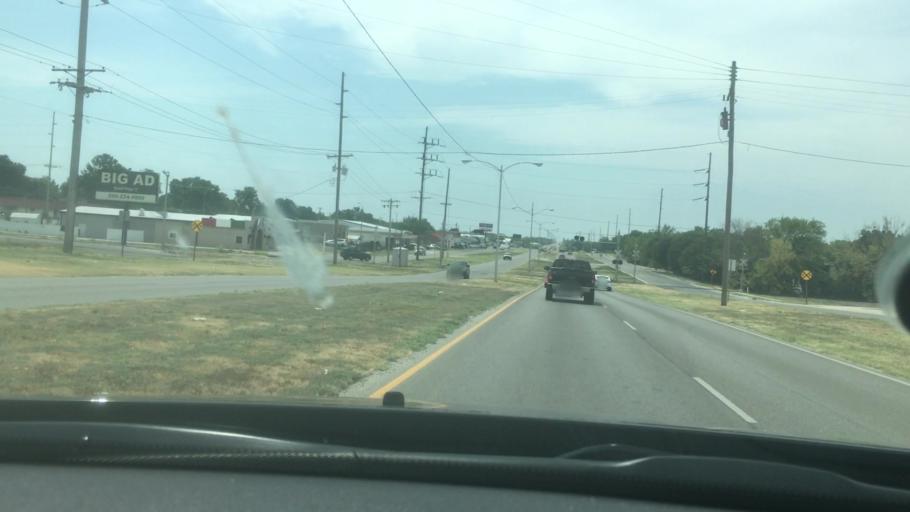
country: US
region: Oklahoma
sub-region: Carter County
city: Ardmore
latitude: 34.1662
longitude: -97.1434
